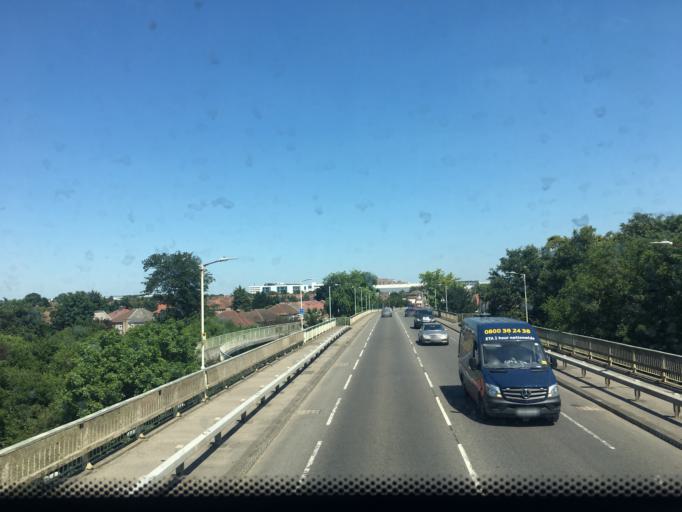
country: GB
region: England
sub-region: Greater London
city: Hayes
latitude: 51.4934
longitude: -0.4288
